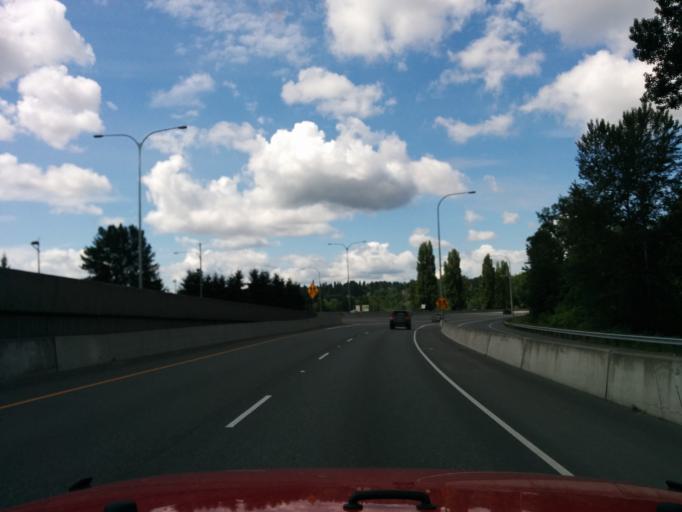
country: US
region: Washington
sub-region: King County
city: Redmond
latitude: 47.6680
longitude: -122.1102
